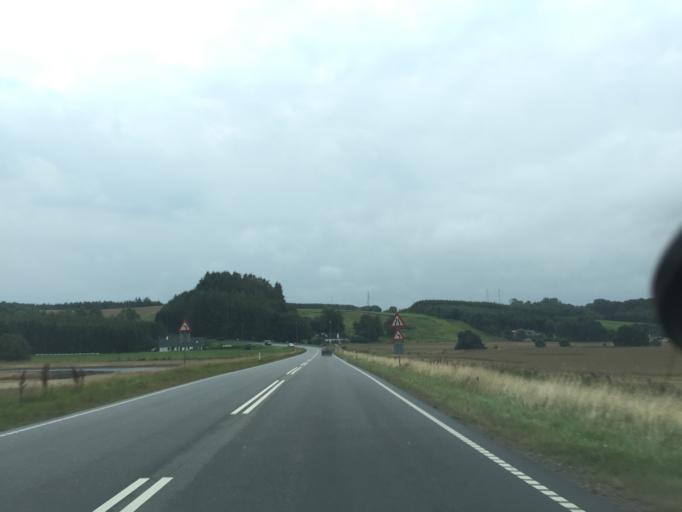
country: DK
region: Central Jutland
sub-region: Skanderborg Kommune
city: Skanderborg
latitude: 56.0563
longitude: 9.9104
